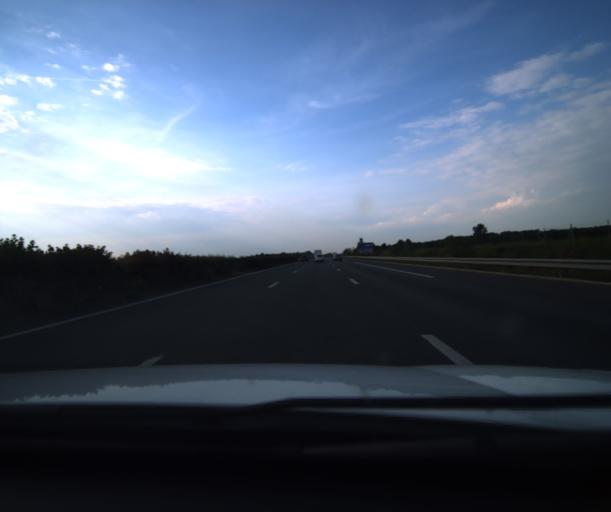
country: FR
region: Midi-Pyrenees
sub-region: Departement du Tarn-et-Garonne
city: Campsas
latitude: 43.8748
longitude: 1.3174
